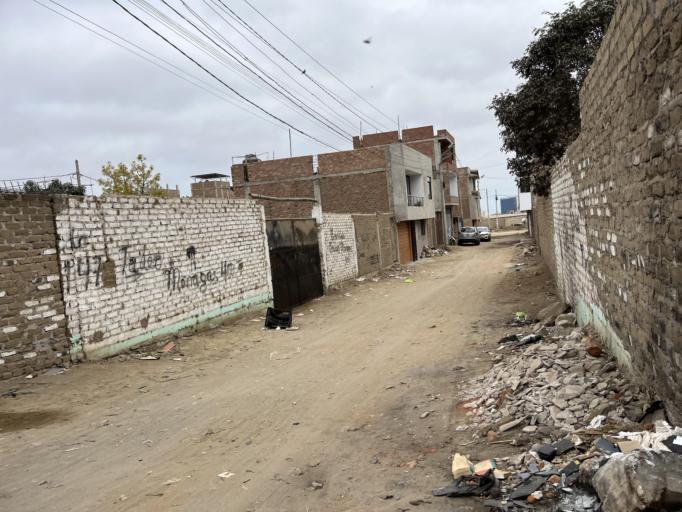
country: PE
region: La Libertad
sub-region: Provincia de Trujillo
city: La Esperanza
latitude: -8.0873
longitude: -79.0345
